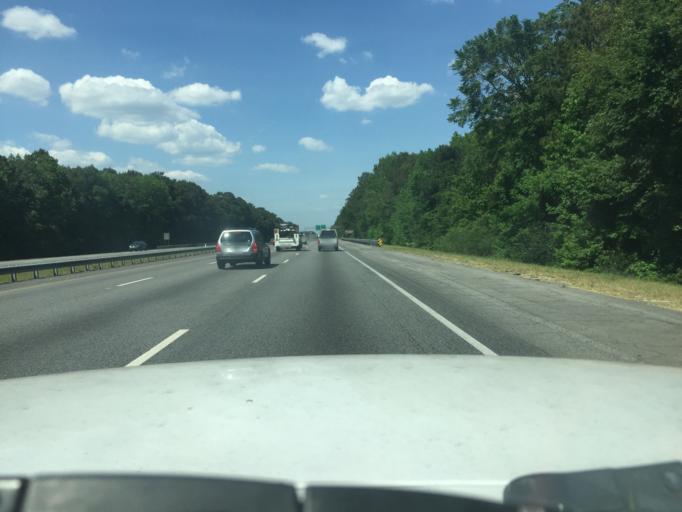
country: US
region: Georgia
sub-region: Chatham County
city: Pooler
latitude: 32.0602
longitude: -81.2528
